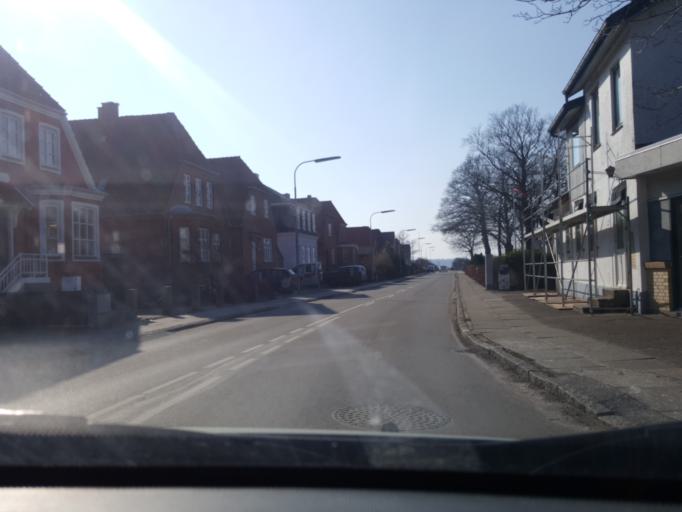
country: DK
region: Zealand
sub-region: Kalundborg Kommune
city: Kalundborg
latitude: 55.6821
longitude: 11.0695
